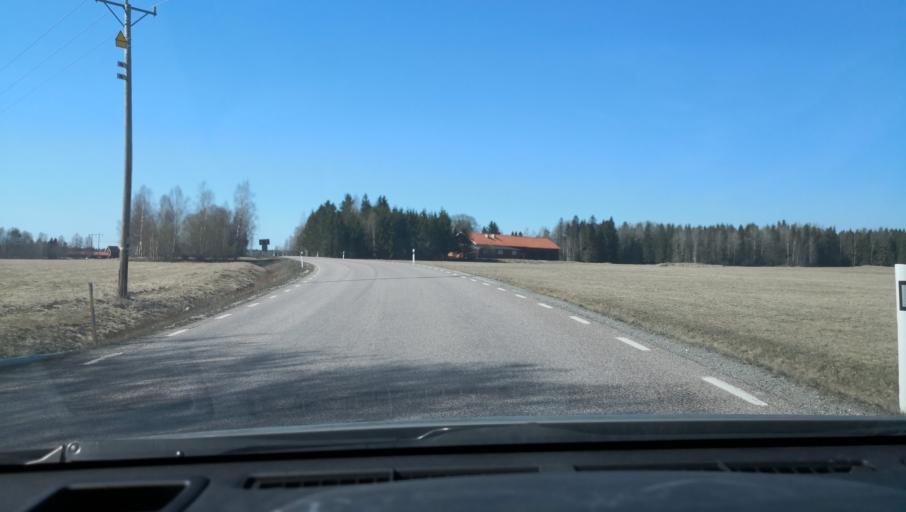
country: SE
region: Vaestmanland
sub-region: Sala Kommun
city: Sala
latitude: 59.9146
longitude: 16.5180
